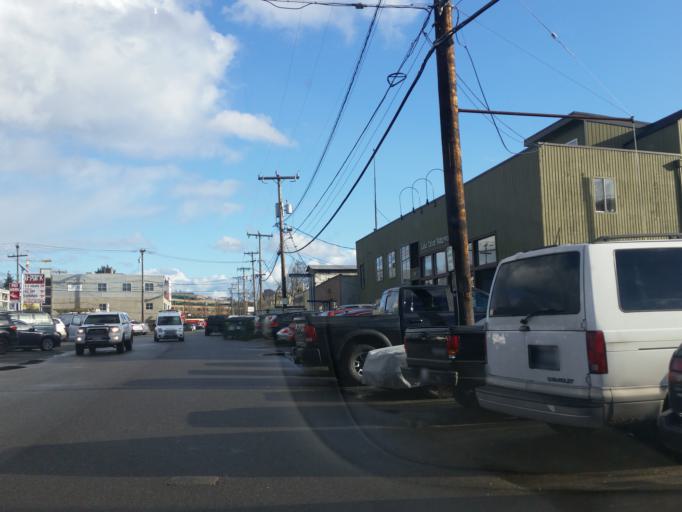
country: US
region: Washington
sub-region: King County
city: Seattle
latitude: 47.6485
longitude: -122.3445
